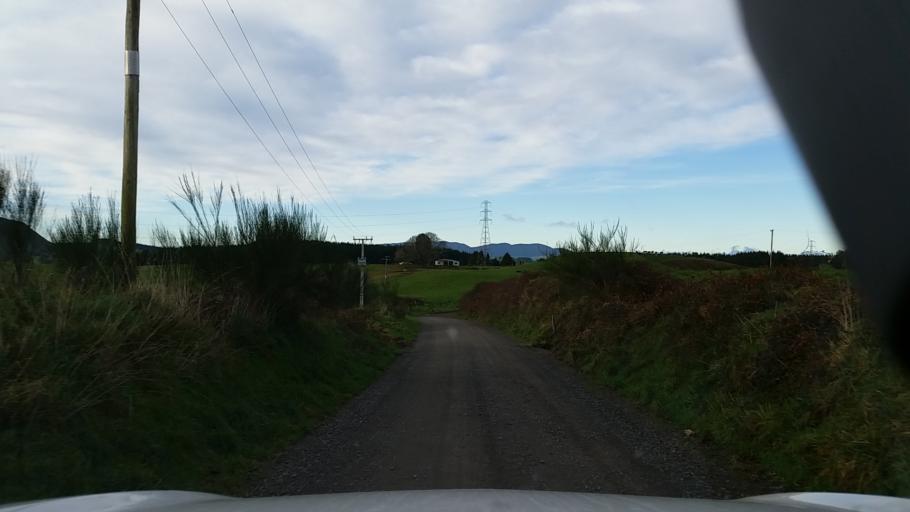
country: NZ
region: Bay of Plenty
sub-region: Rotorua District
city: Rotorua
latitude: -38.2263
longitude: 176.1622
